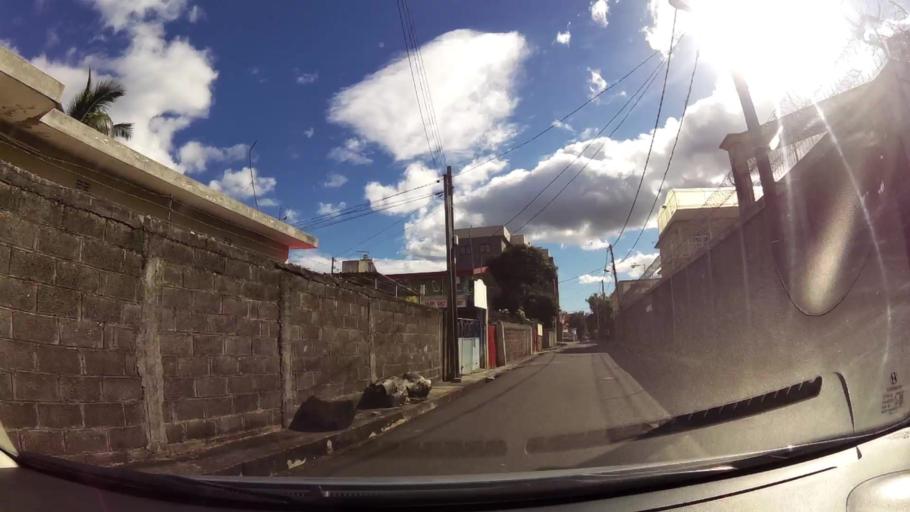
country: MU
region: Port Louis
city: Port Louis
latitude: -20.1494
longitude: 57.5103
